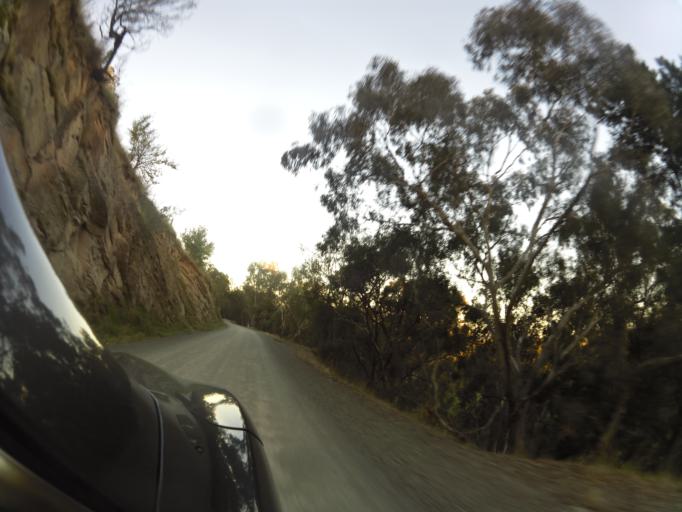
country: AU
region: Victoria
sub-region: Murrindindi
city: Alexandra
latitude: -37.1537
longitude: 145.5360
